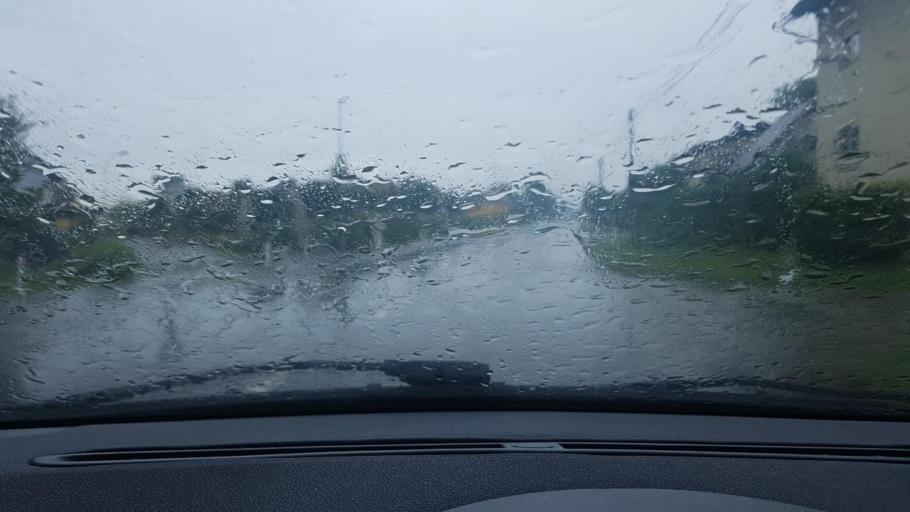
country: AT
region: Styria
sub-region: Politischer Bezirk Graz-Umgebung
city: Zettling
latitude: 46.9538
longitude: 15.4316
